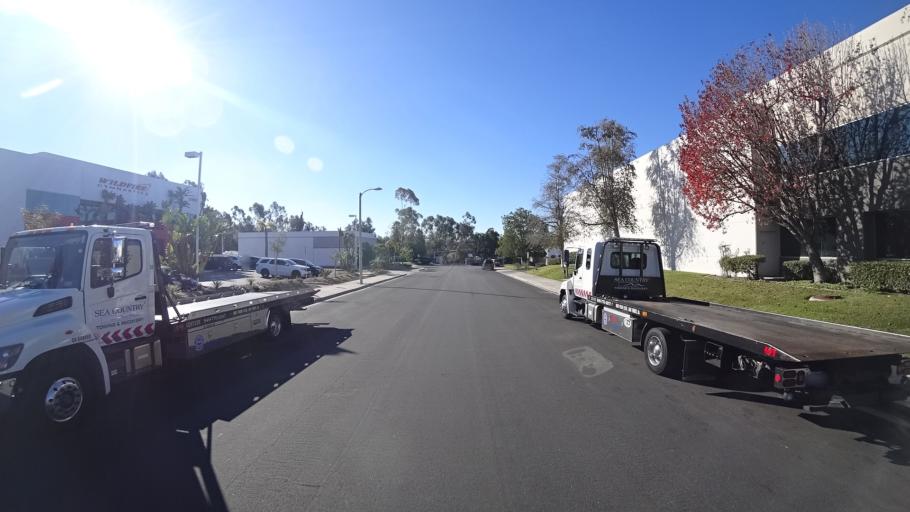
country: US
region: California
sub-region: Orange County
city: Lake Forest
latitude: 33.6623
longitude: -117.6752
